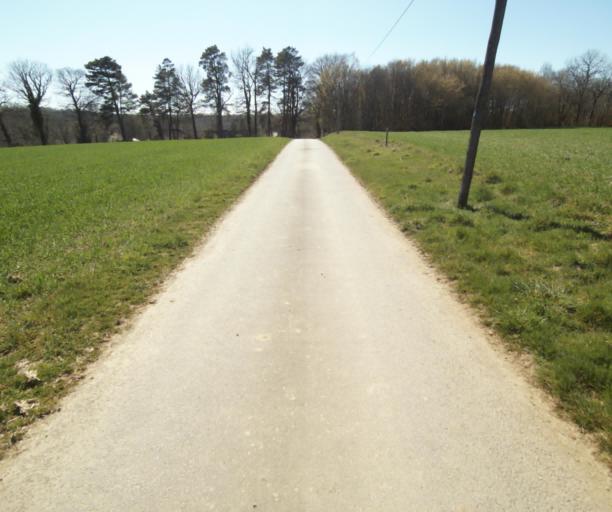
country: FR
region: Limousin
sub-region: Departement de la Correze
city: Chamboulive
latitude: 45.4542
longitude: 1.7190
